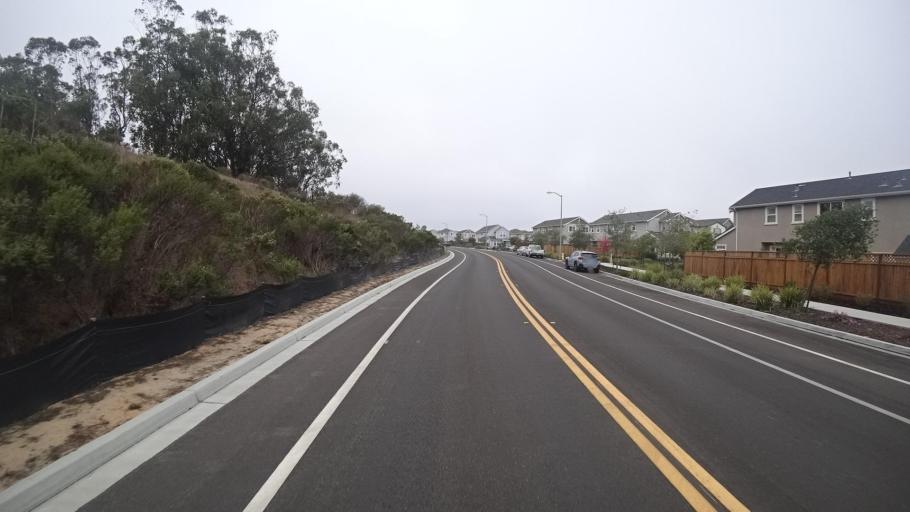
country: US
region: California
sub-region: Monterey County
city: Marina
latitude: 36.6511
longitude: -121.7378
